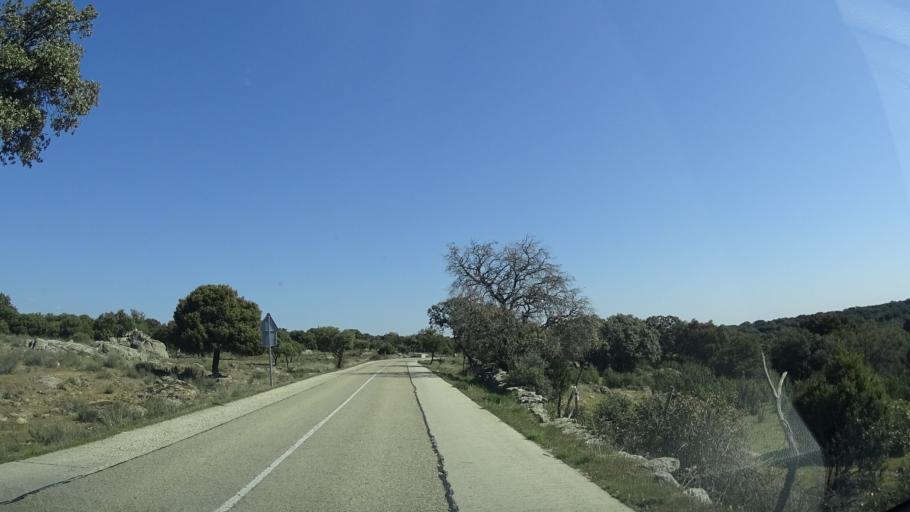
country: ES
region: Madrid
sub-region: Provincia de Madrid
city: Hoyo de Manzanares
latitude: 40.6422
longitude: -3.8465
